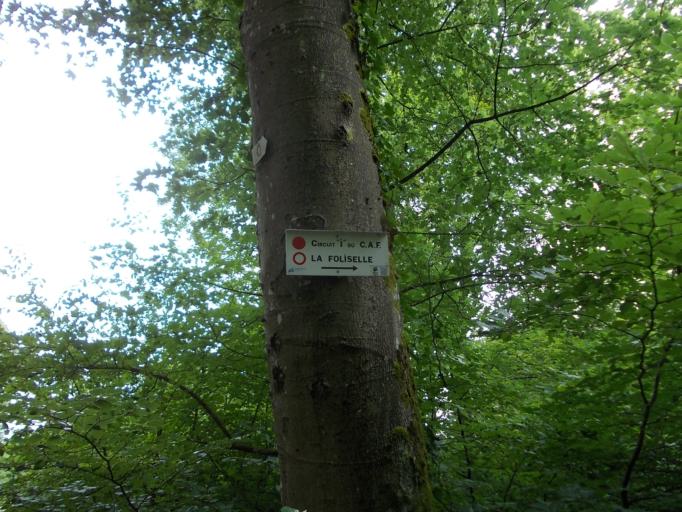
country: FR
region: Lorraine
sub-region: Departement de Meurthe-et-Moselle
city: Faulx
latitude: 48.7785
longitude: 6.1831
